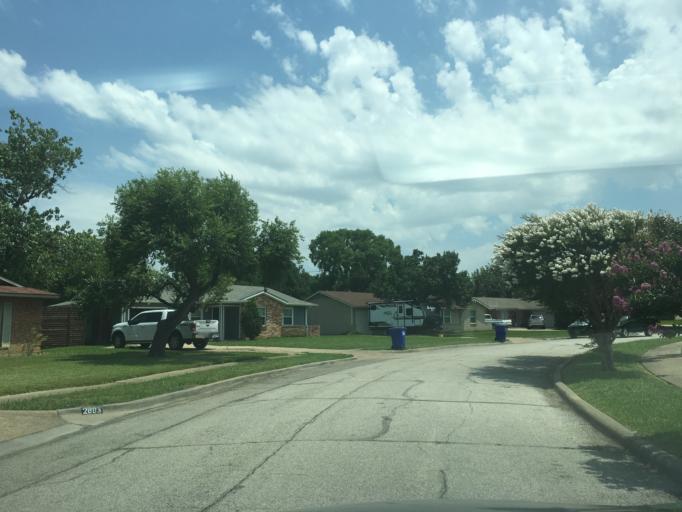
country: US
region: Texas
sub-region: Dallas County
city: Carrollton
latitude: 32.9413
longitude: -96.8806
